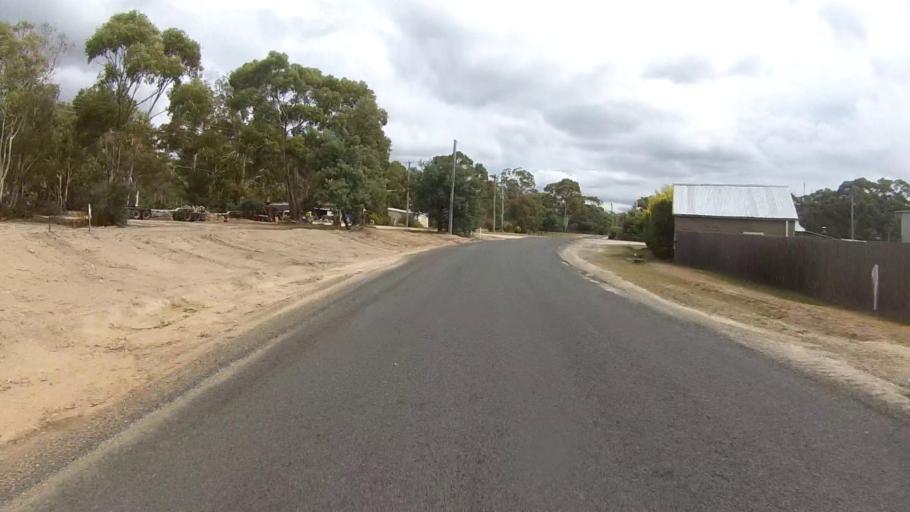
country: AU
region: Tasmania
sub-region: Break O'Day
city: St Helens
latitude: -41.8216
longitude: 147.8964
